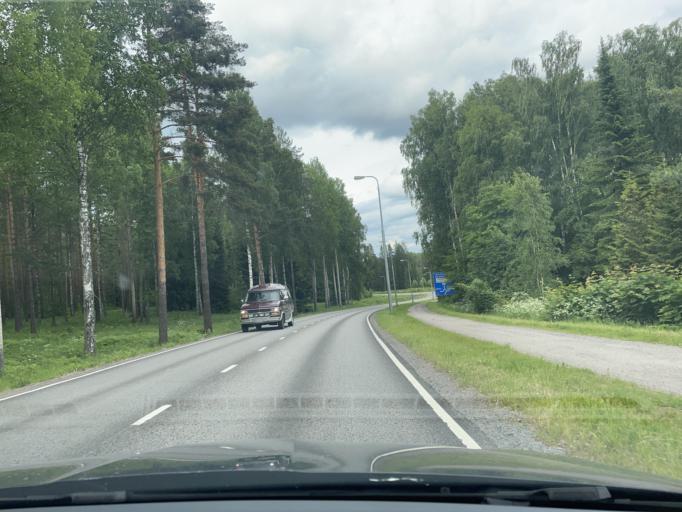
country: FI
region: Central Finland
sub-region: Jaemsae
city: Jaemsaenkoski
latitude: 61.9213
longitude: 25.1529
